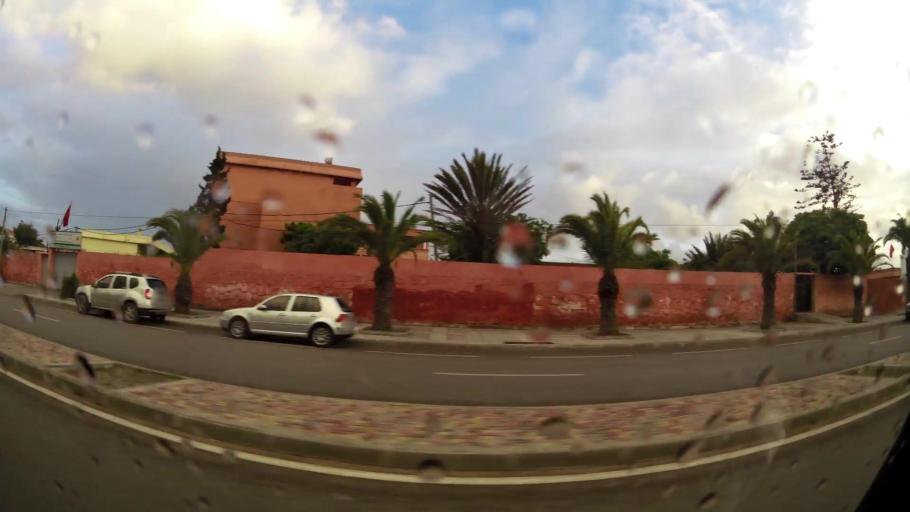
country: MA
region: Doukkala-Abda
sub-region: El-Jadida
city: El Jadida
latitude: 33.2415
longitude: -8.5012
